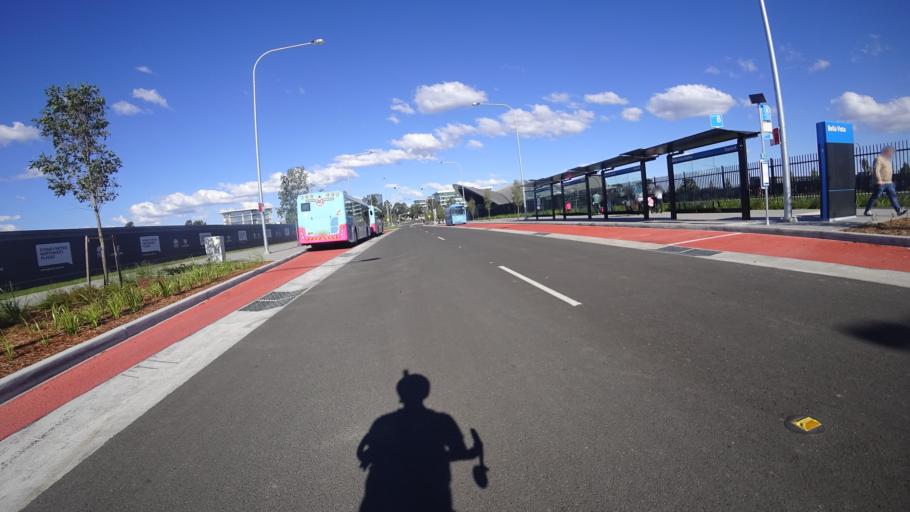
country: AU
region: New South Wales
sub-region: Blacktown
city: Stanhope Gardens
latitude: -33.7302
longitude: 150.9442
